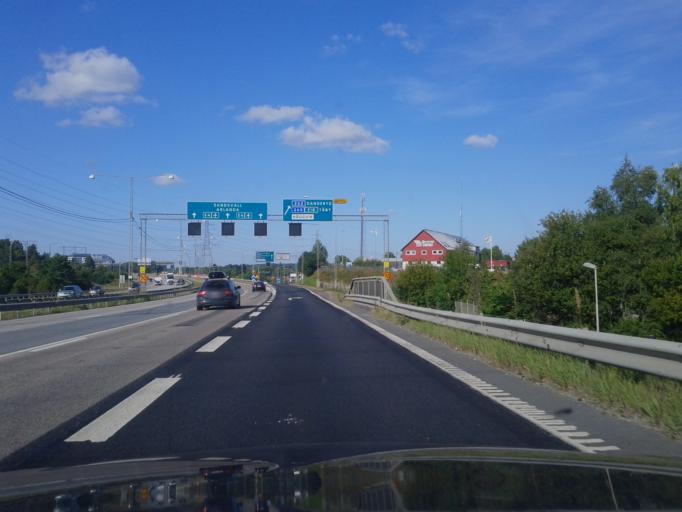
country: SE
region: Stockholm
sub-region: Sollentuna Kommun
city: Sollentuna
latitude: 59.4336
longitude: 17.9233
